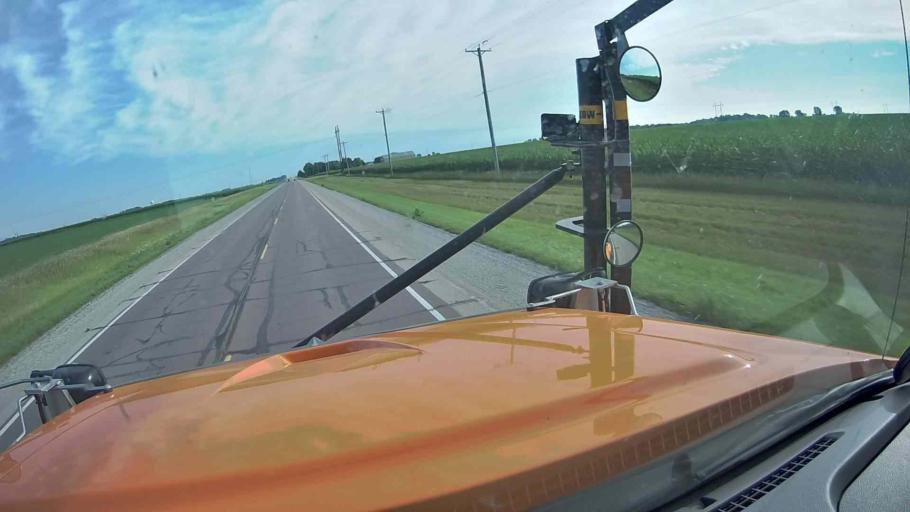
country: US
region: Iowa
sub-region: Cerro Gordo County
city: Mason City
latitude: 43.0878
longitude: -93.2014
